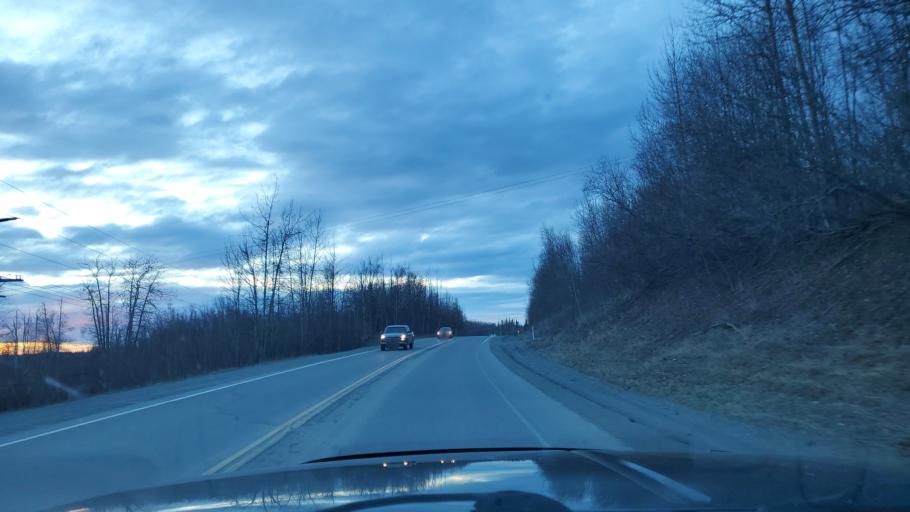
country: US
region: Alaska
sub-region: Matanuska-Susitna Borough
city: Lakes
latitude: 61.6061
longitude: -149.3428
